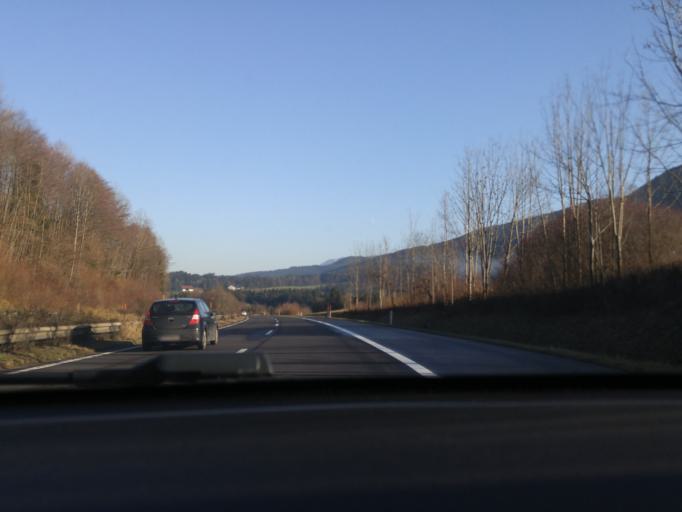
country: AT
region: Upper Austria
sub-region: Politischer Bezirk Vocklabruck
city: Innerschwand
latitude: 47.8361
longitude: 13.4155
